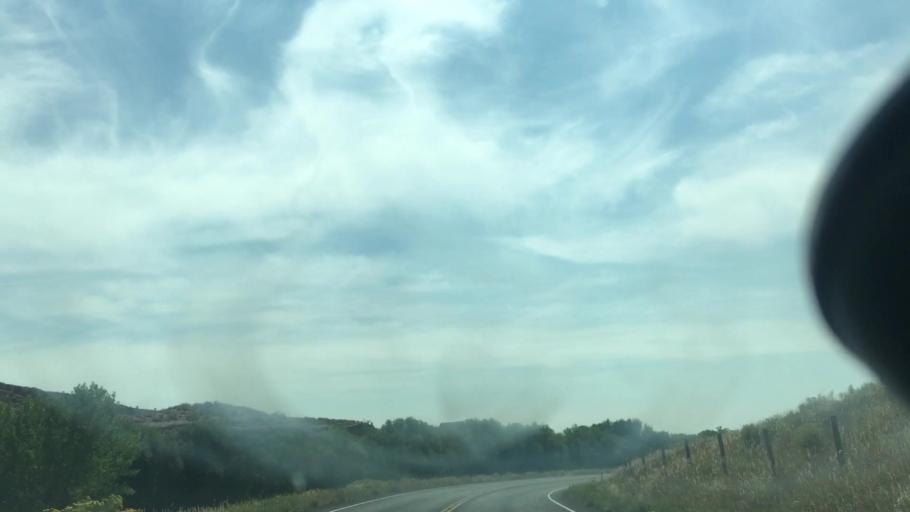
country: US
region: Colorado
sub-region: Larimer County
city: Laporte
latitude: 40.5200
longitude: -105.2513
